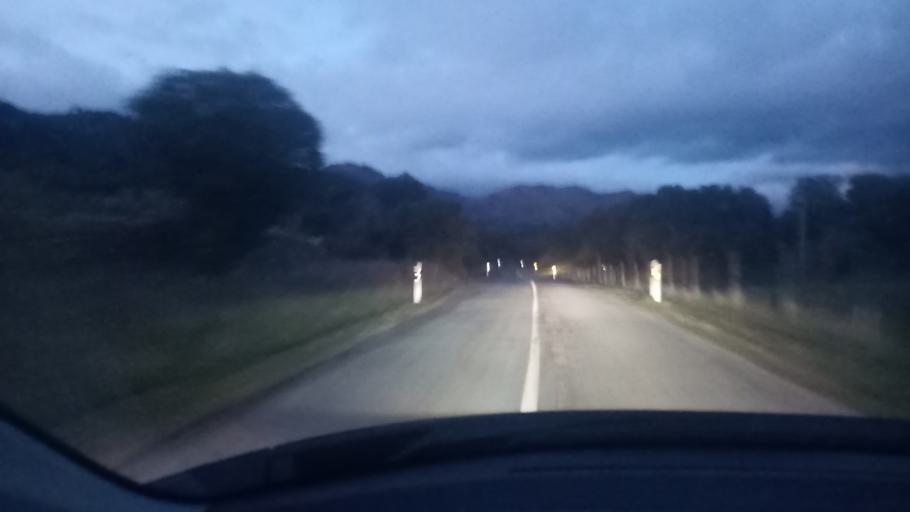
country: ES
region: Madrid
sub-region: Provincia de Madrid
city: Colmenar del Arroyo
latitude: 40.4381
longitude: -4.2426
